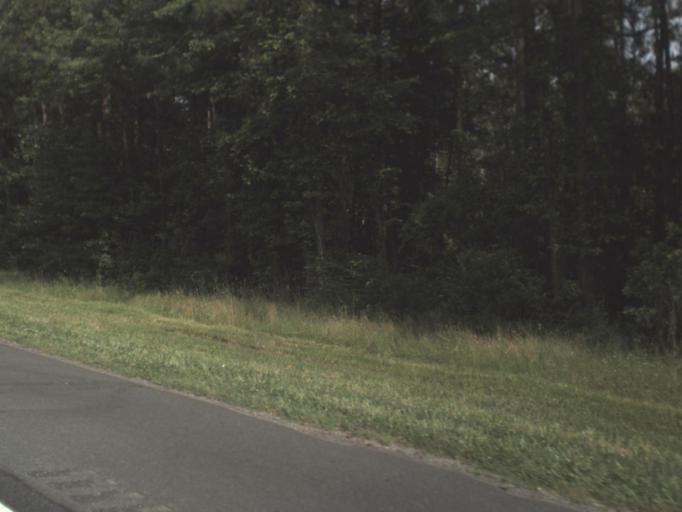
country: US
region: Florida
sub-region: Baker County
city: Macclenny
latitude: 30.2683
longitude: -82.0914
